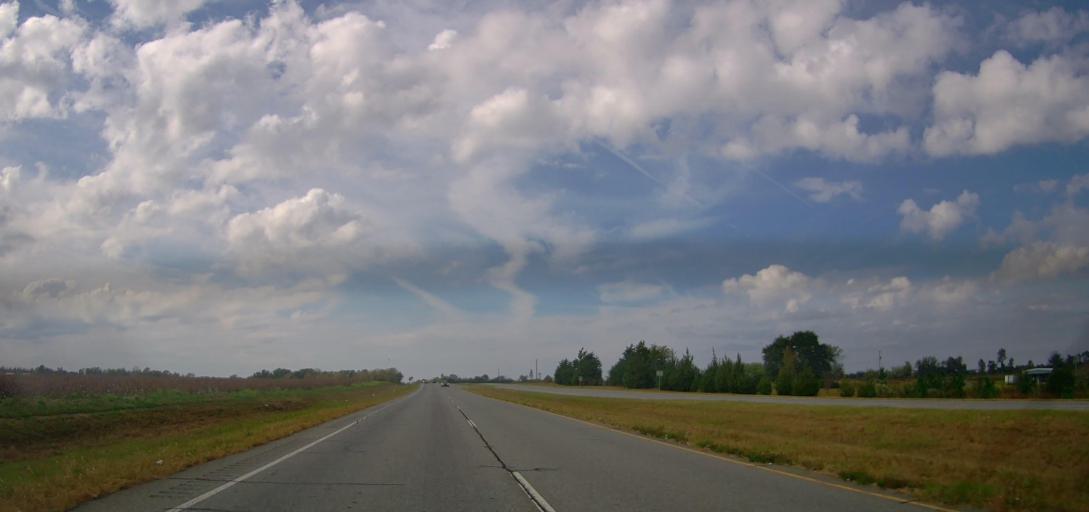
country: US
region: Georgia
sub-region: Mitchell County
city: Pelham
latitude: 31.1099
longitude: -84.1203
